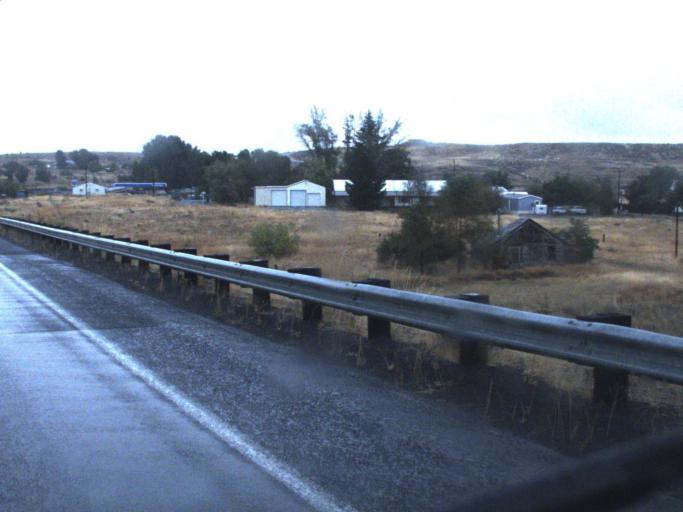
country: US
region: Washington
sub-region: Lincoln County
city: Davenport
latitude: 47.2950
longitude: -117.9731
